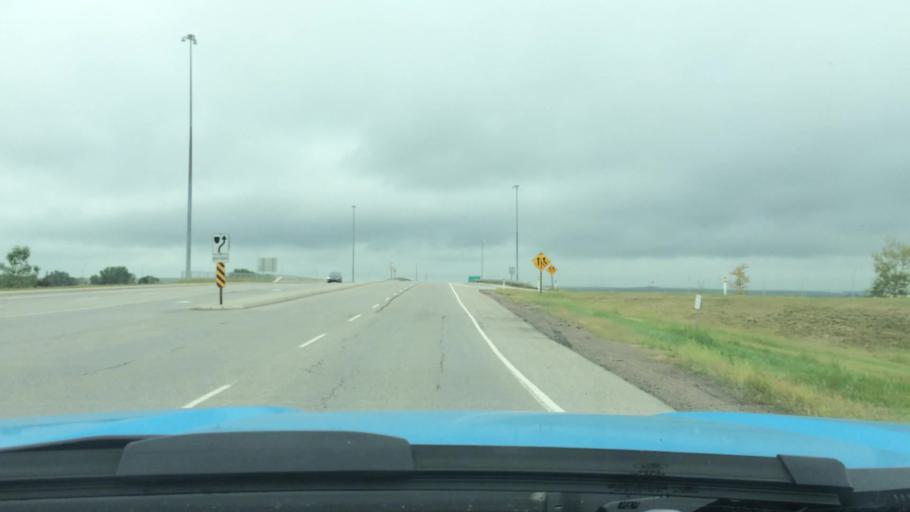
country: CA
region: Alberta
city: Airdrie
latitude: 51.3001
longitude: -113.9986
